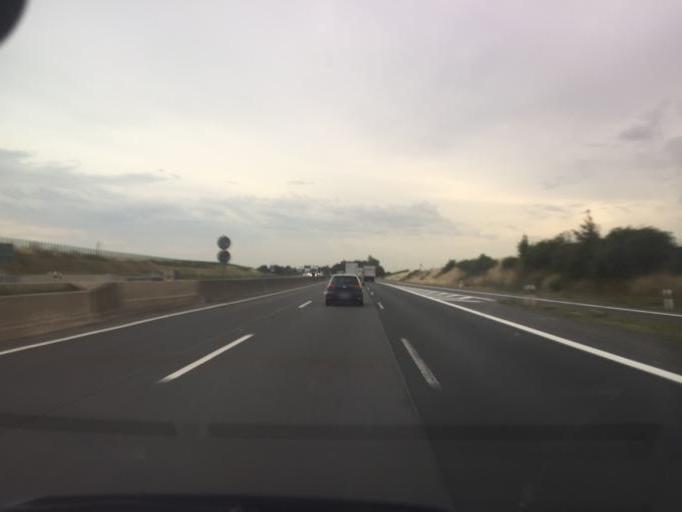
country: DE
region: North Rhine-Westphalia
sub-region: Regierungsbezirk Dusseldorf
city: Juchen
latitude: 51.0901
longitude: 6.4206
